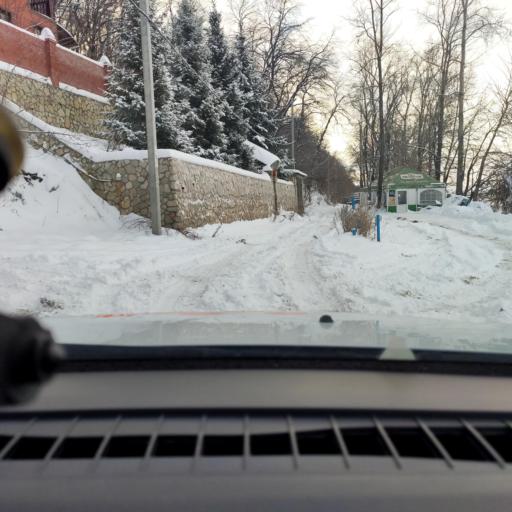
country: RU
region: Samara
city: Samara
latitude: 53.2896
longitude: 50.1918
